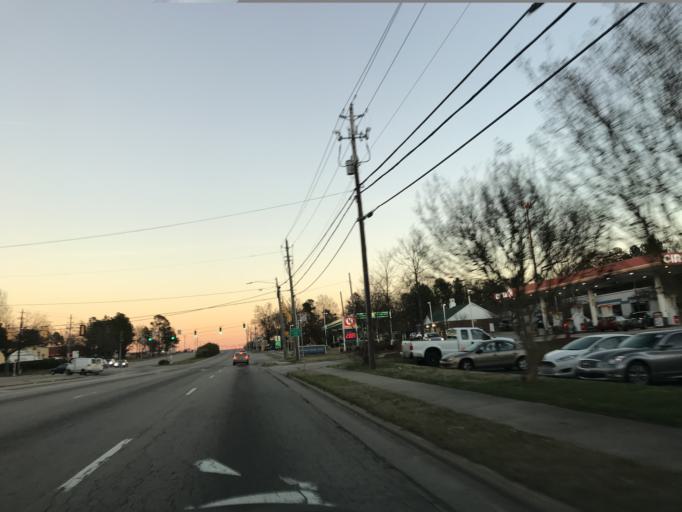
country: US
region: North Carolina
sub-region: Wake County
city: Raleigh
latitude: 35.7990
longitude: -78.5694
